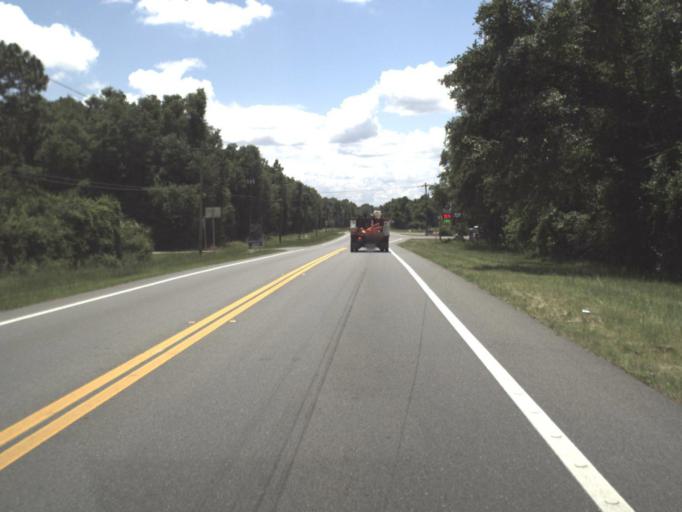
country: US
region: Florida
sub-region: Clay County
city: Keystone Heights
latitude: 29.7632
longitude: -82.0037
